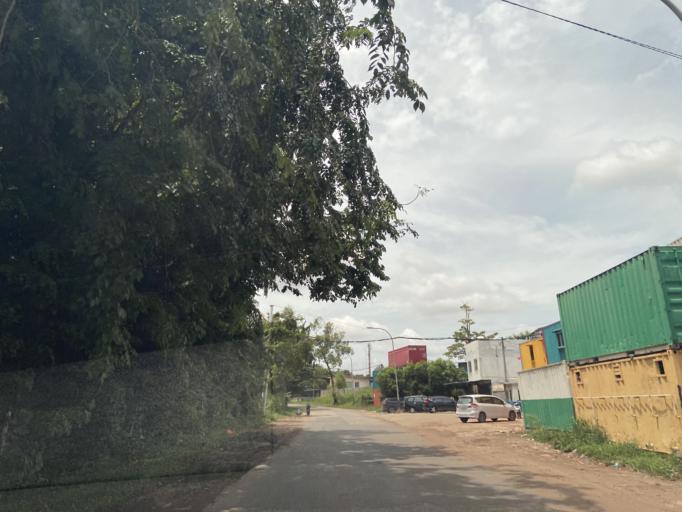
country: SG
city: Singapore
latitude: 1.1599
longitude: 104.0050
